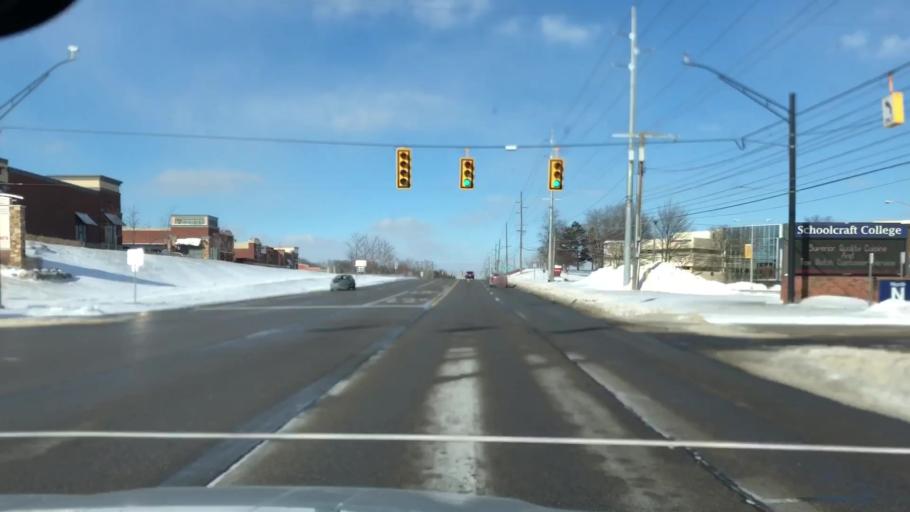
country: US
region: Michigan
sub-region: Wayne County
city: Northville
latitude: 42.4221
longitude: -83.4329
